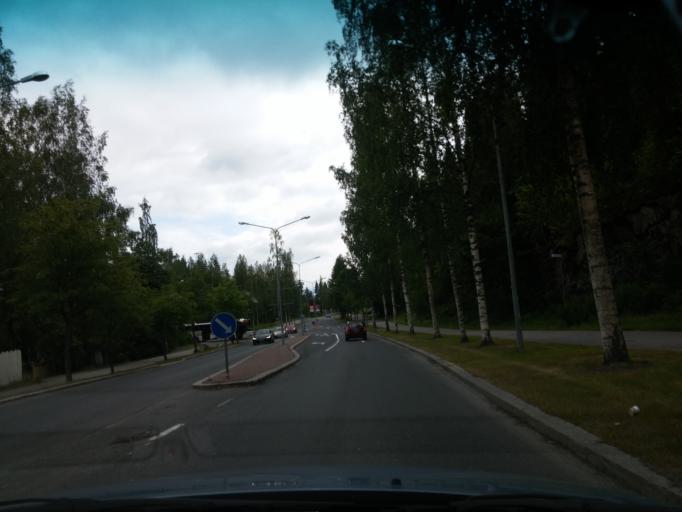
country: FI
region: Northern Savo
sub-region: Kuopio
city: Kuopio
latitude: 62.8349
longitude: 27.6135
